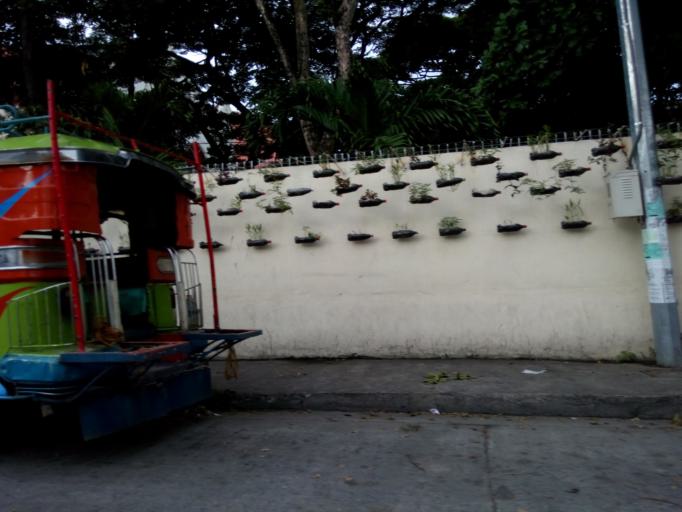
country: PH
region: Central Visayas
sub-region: Province of Negros Oriental
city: Dumaguete
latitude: 9.3103
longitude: 123.3053
